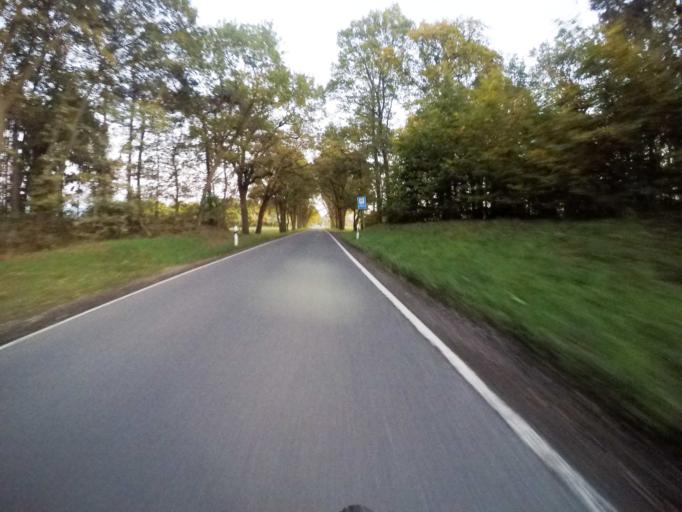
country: DE
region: North Rhine-Westphalia
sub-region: Regierungsbezirk Dusseldorf
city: Bocholt
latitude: 51.7933
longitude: 6.5842
